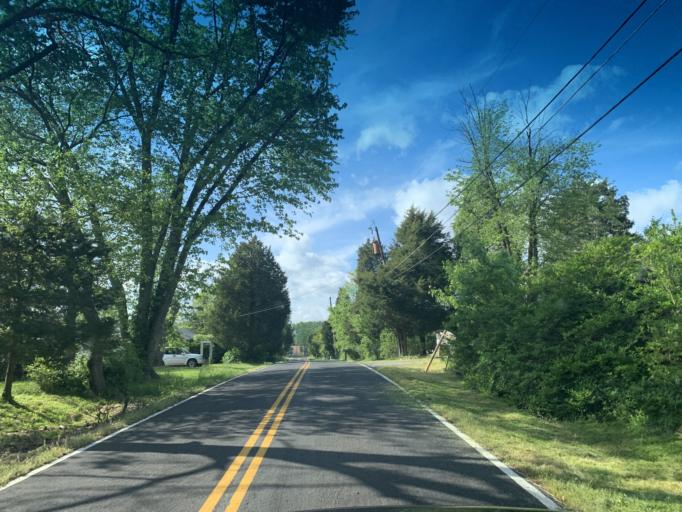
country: US
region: Maryland
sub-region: Cecil County
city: Rising Sun
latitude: 39.6964
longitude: -76.1999
